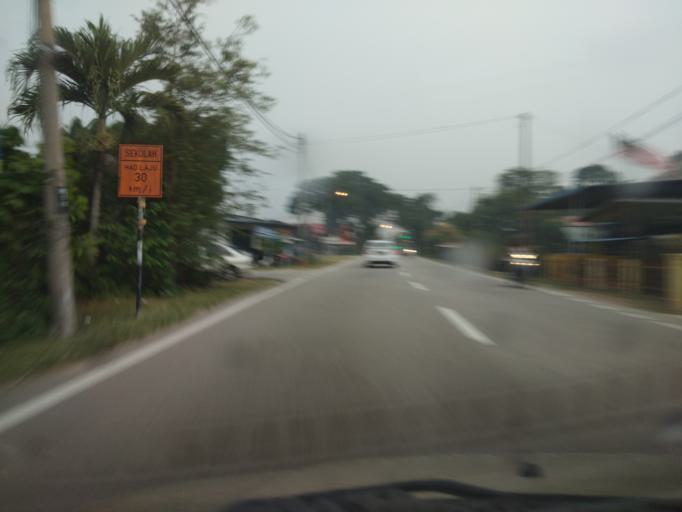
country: MY
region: Penang
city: Permatang Kuching
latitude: 5.4800
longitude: 100.4014
